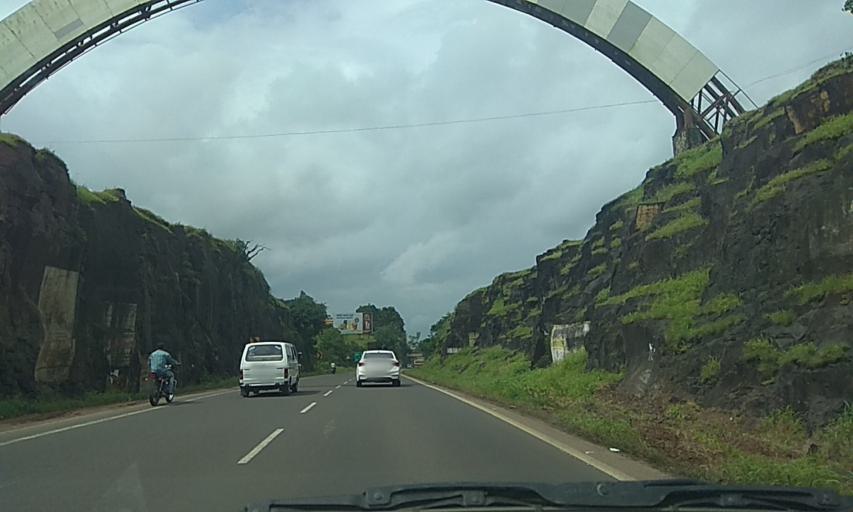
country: IN
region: Maharashtra
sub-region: Kolhapur
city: Kolhapur
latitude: 16.6596
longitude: 74.2671
